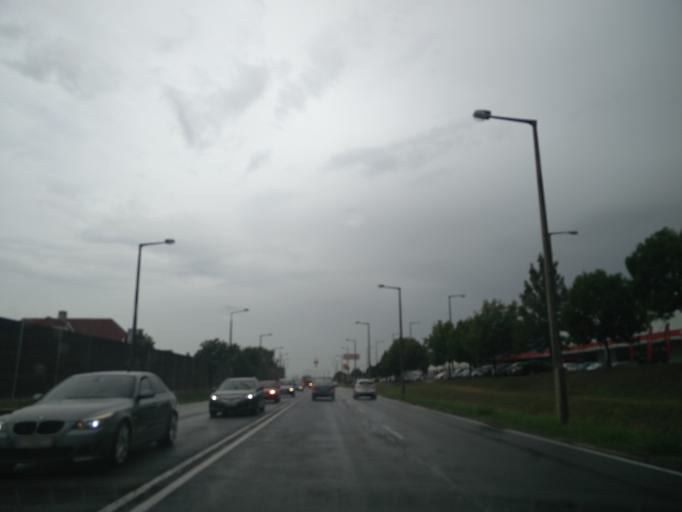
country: HU
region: Fejer
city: Szekesfehervar
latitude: 47.2059
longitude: 18.4278
